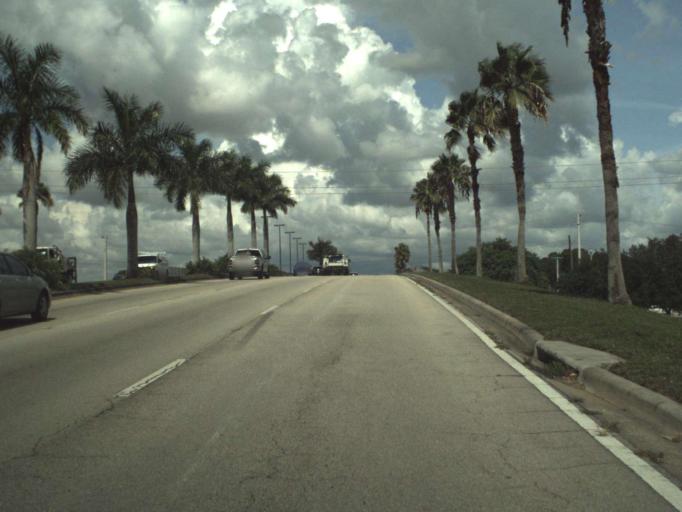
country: US
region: Florida
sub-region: Saint Lucie County
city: River Park
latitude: 27.3179
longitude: -80.3727
